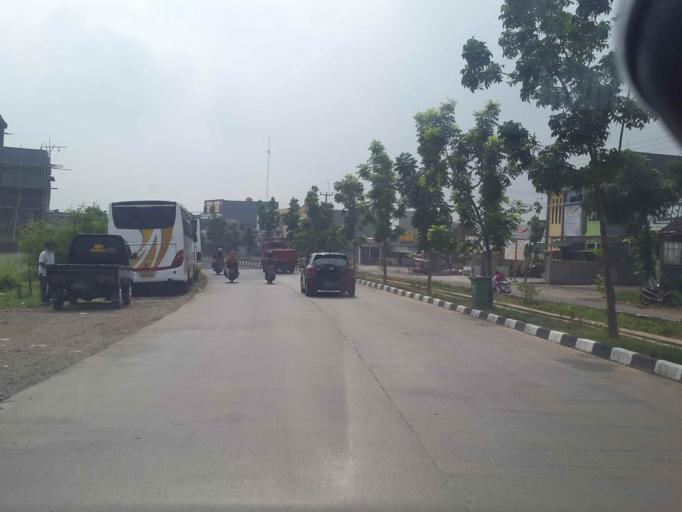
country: ID
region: West Java
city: Cikarang
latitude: -6.3362
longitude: 107.2780
